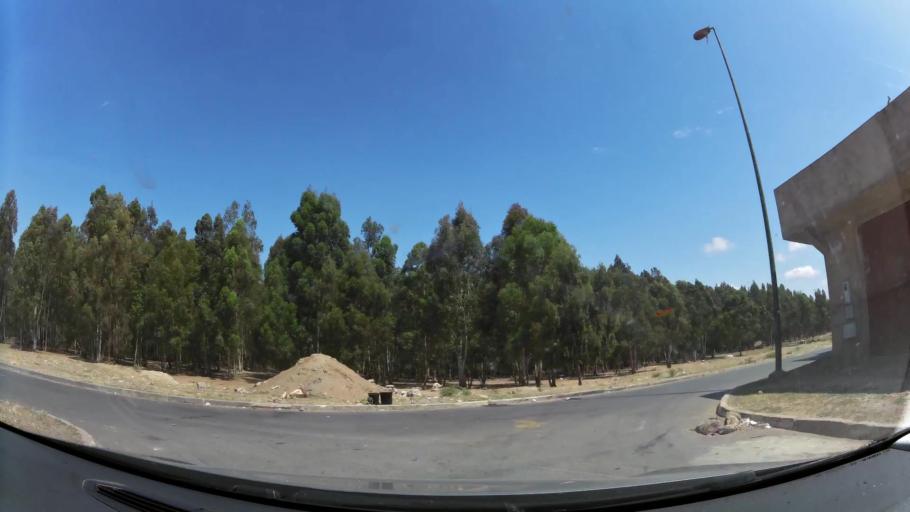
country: MA
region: Gharb-Chrarda-Beni Hssen
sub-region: Kenitra Province
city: Kenitra
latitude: 34.2451
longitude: -6.5364
